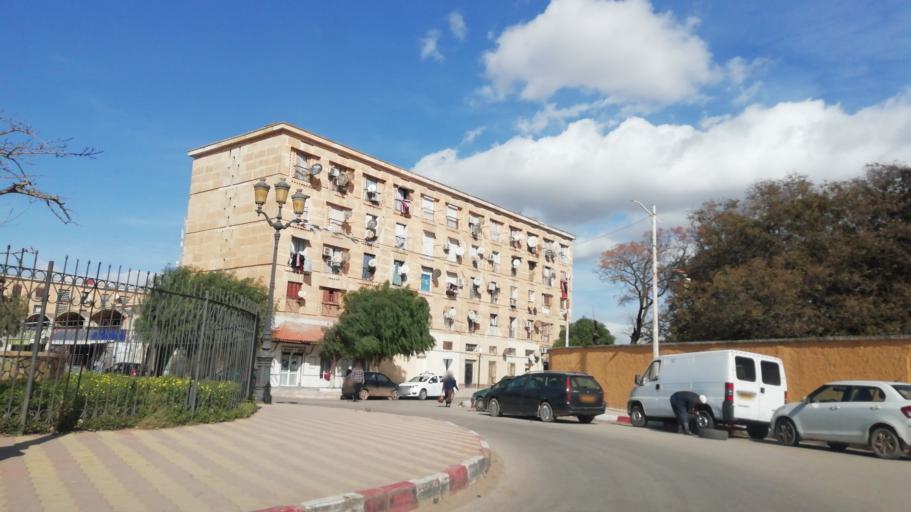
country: DZ
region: Oran
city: Es Senia
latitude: 35.6100
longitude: -0.5767
